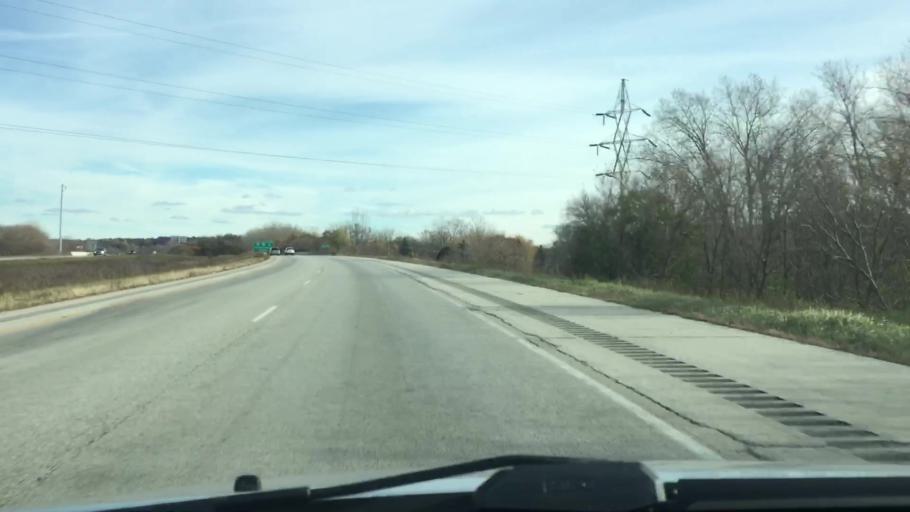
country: US
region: Wisconsin
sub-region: Brown County
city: Green Bay
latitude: 44.5204
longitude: -87.9703
